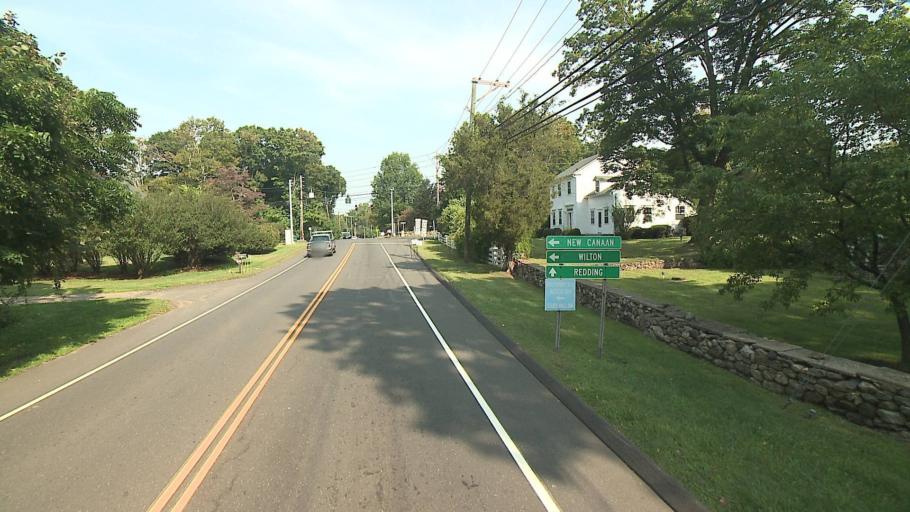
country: US
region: Connecticut
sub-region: Fairfield County
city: Wilton
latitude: 41.2004
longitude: -73.3802
